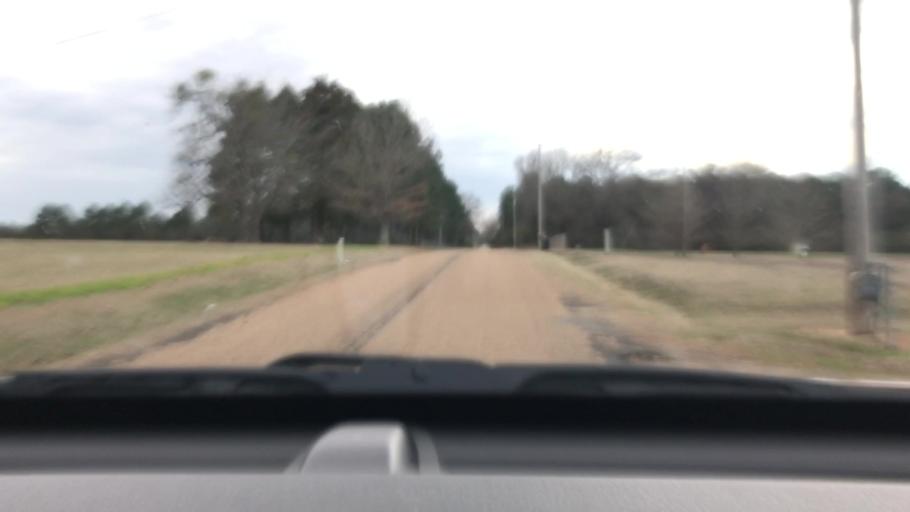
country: US
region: Arkansas
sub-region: Hempstead County
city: Hope
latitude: 33.6387
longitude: -93.5673
